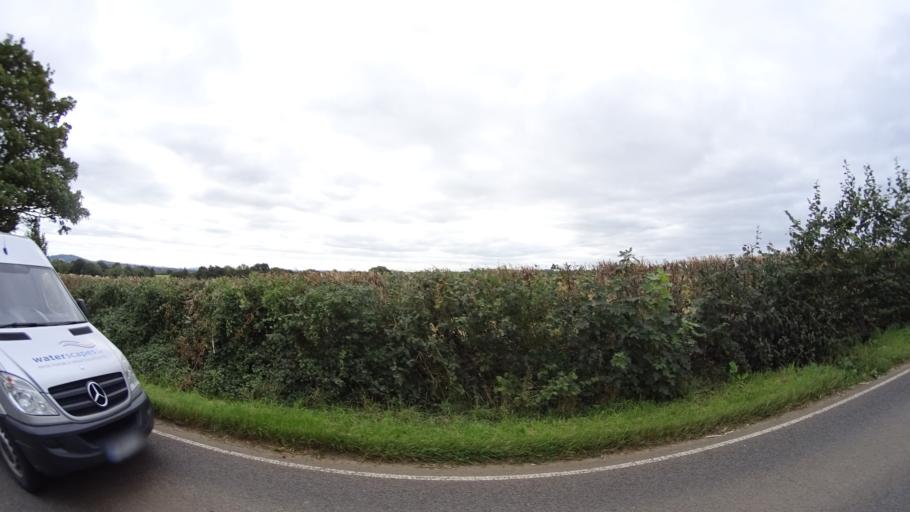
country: GB
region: England
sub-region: Dorset
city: Gillingham
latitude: 51.0466
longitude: -2.3179
